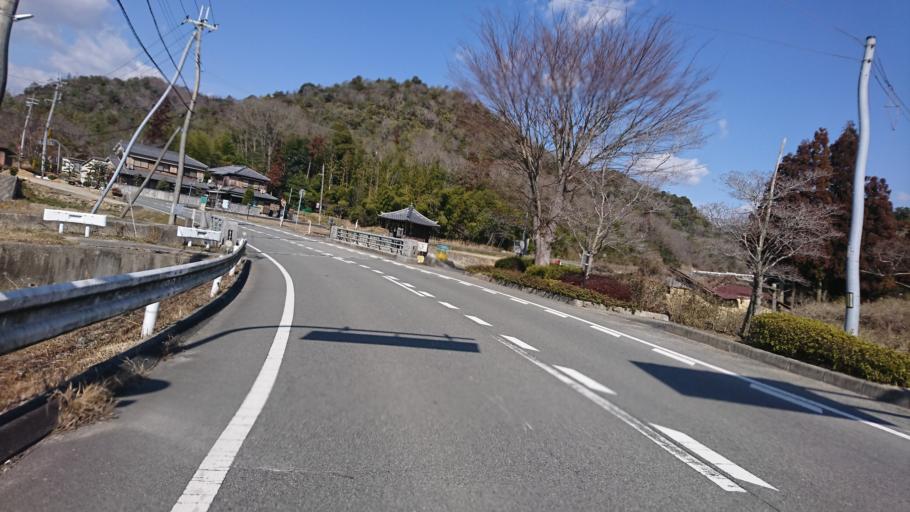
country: JP
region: Hyogo
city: Kakogawacho-honmachi
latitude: 34.8535
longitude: 134.8099
